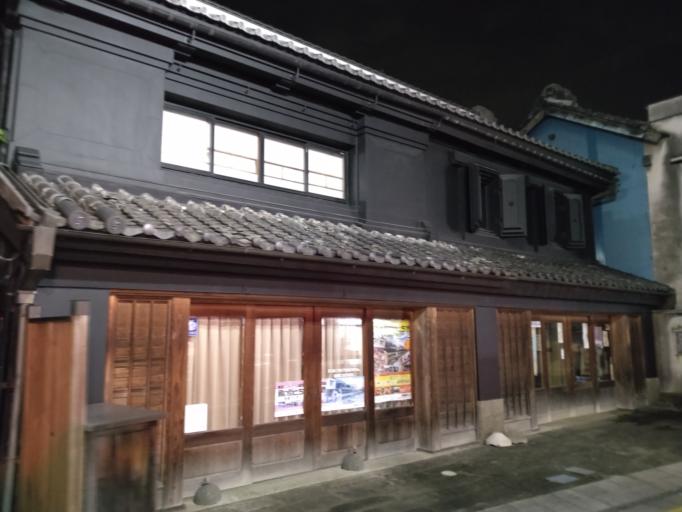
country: JP
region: Tochigi
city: Tochigi
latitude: 36.3811
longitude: 139.7342
